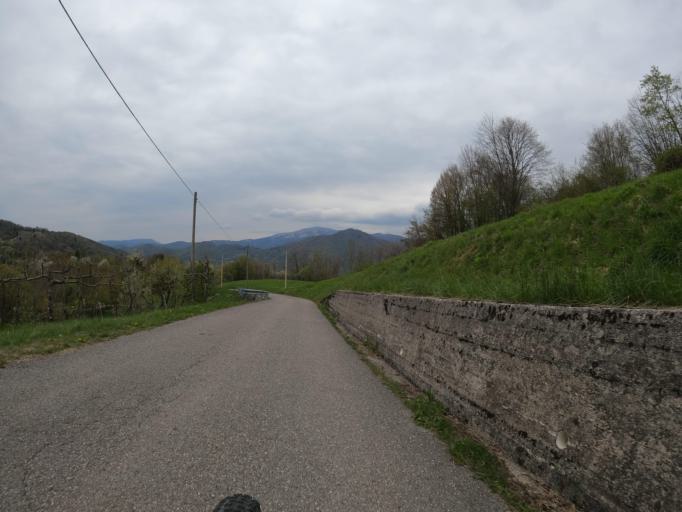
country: IT
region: Friuli Venezia Giulia
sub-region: Provincia di Udine
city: Clodig
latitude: 46.1436
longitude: 13.6142
